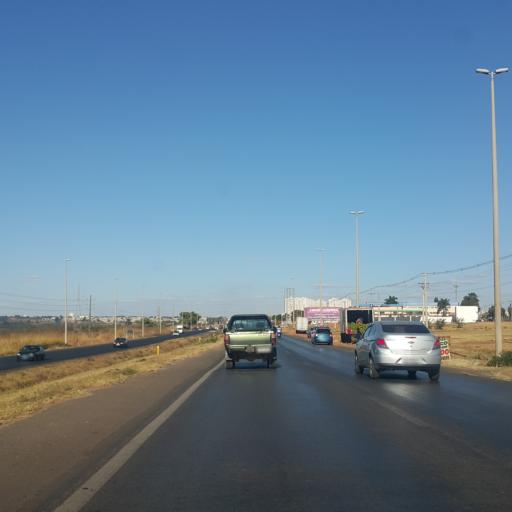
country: BR
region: Federal District
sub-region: Brasilia
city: Brasilia
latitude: -15.7903
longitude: -48.1079
